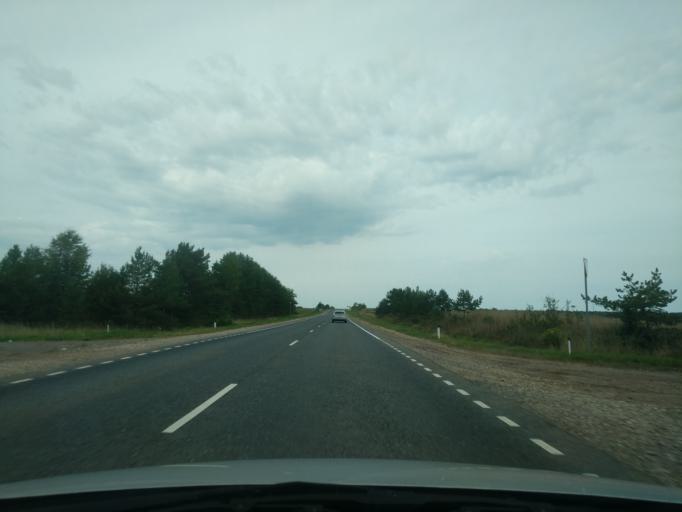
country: RU
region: Kirov
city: Mirnyy
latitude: 58.2683
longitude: 47.8193
